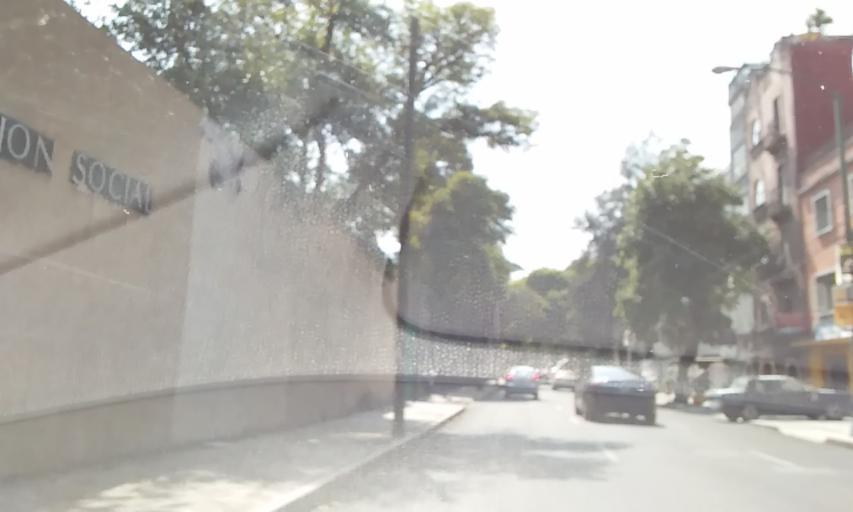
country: MX
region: Mexico City
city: Cuauhtemoc
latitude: 19.4332
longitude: -99.1645
